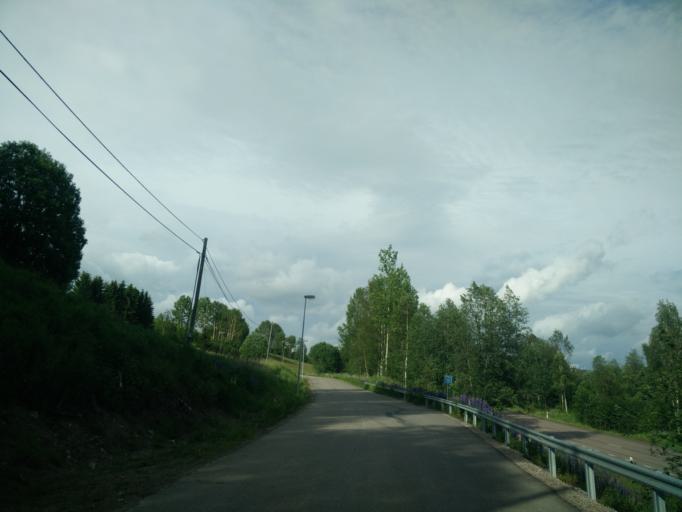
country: SE
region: Vaesternorrland
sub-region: Sundsvalls Kommun
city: Sundsvall
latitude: 62.4196
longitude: 17.2426
